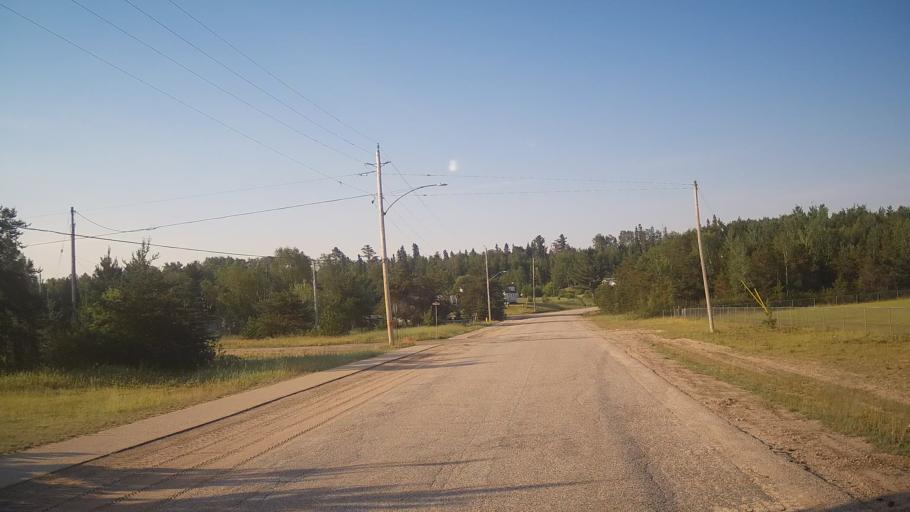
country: CA
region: Ontario
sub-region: Rainy River District
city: Atikokan
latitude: 49.4043
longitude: -91.6567
